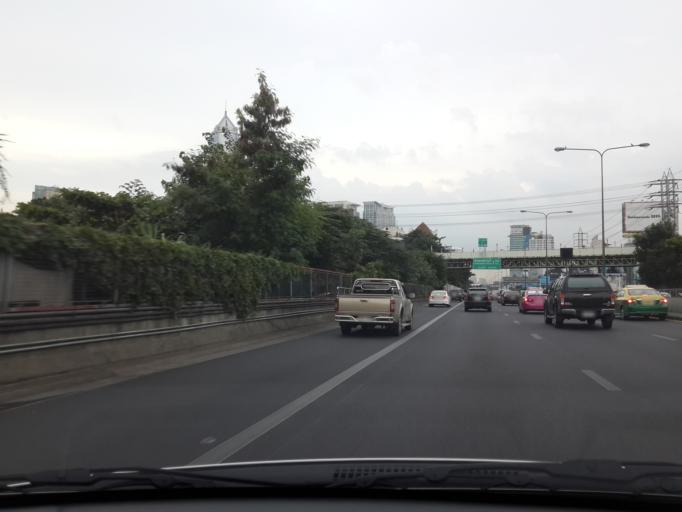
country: TH
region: Bangkok
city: Khlong Toei
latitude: 13.7326
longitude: 100.5516
